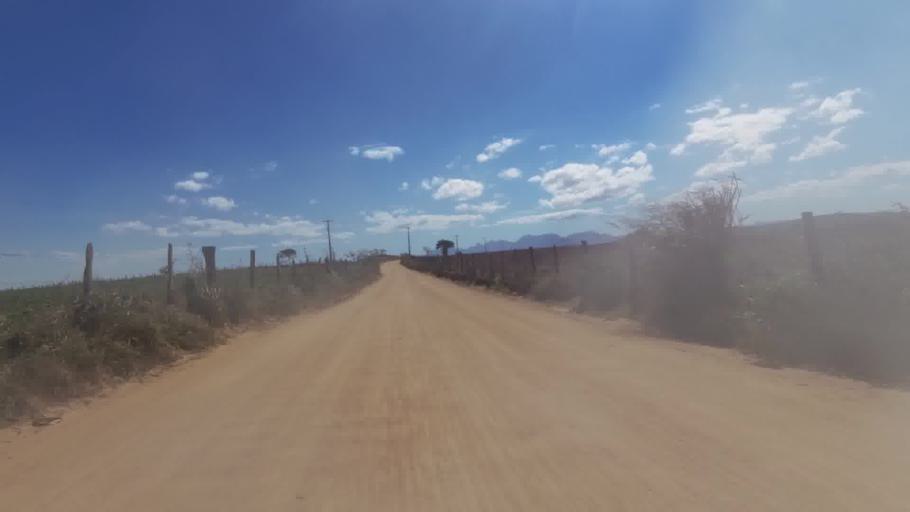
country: BR
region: Espirito Santo
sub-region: Marataizes
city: Marataizes
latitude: -21.1570
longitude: -40.9781
